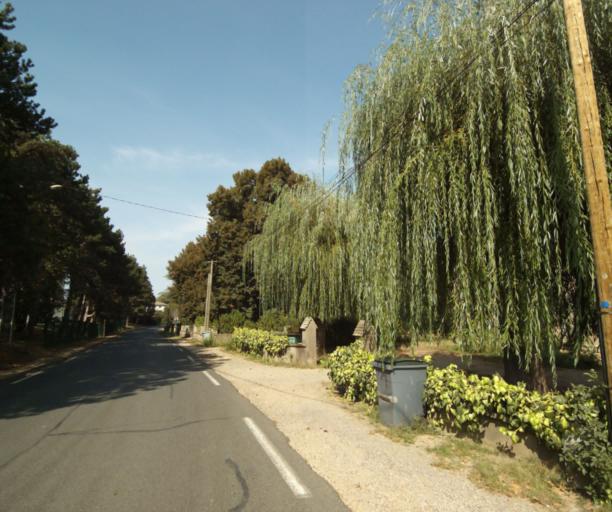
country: FR
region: Bourgogne
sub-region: Departement de Saone-et-Loire
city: Tournus
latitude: 46.5520
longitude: 4.9011
